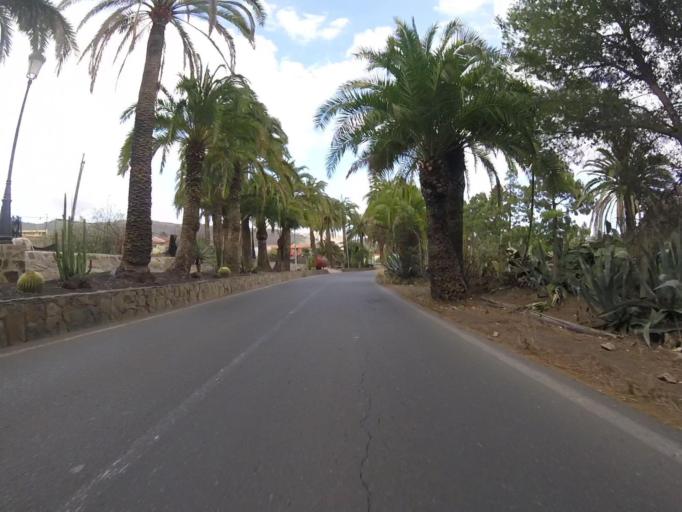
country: ES
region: Canary Islands
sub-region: Provincia de Las Palmas
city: Santa Brigida
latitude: 28.0365
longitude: -15.4955
